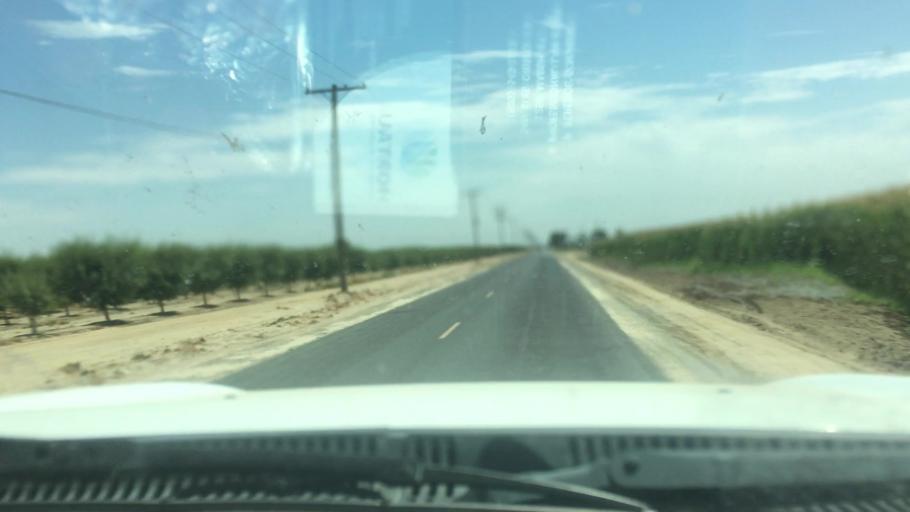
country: US
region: California
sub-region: Tulare County
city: Tipton
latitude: 36.0571
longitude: -119.3220
